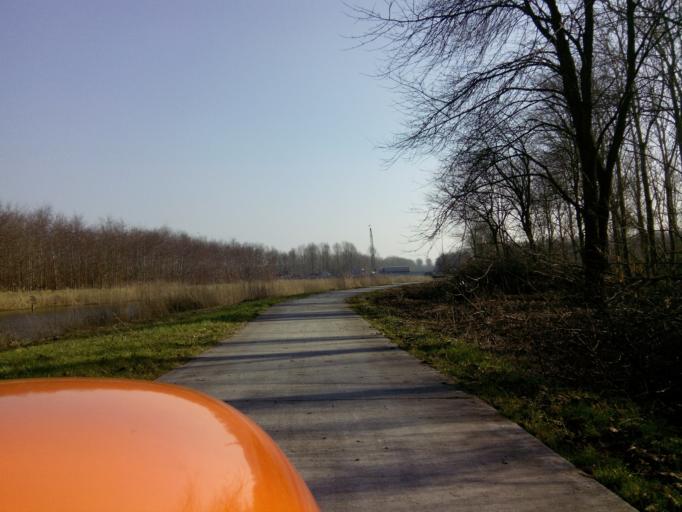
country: NL
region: Flevoland
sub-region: Gemeente Zeewolde
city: Zeewolde
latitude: 52.3421
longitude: 5.4847
